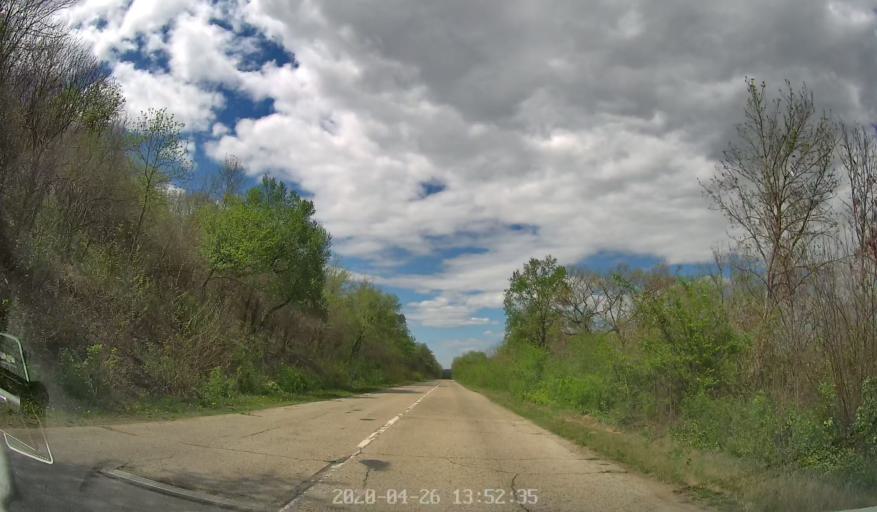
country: MD
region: Telenesti
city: Cocieri
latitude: 47.2733
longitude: 29.1173
